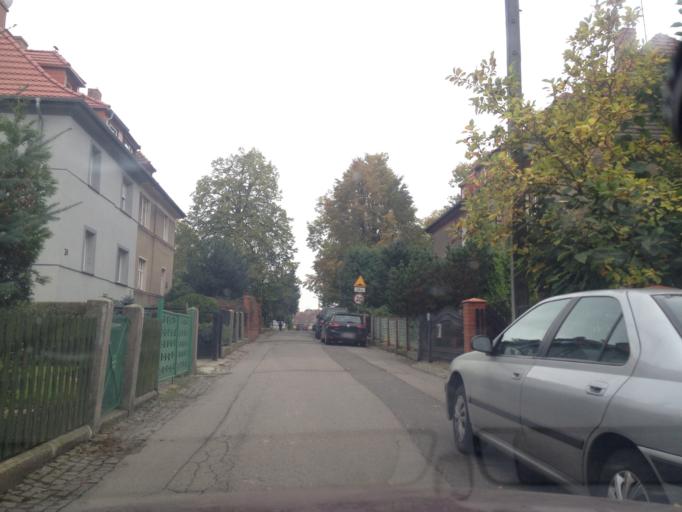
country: PL
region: Lower Silesian Voivodeship
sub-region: Powiat zgorzelecki
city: Zgorzelec
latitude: 51.1553
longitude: 15.0103
